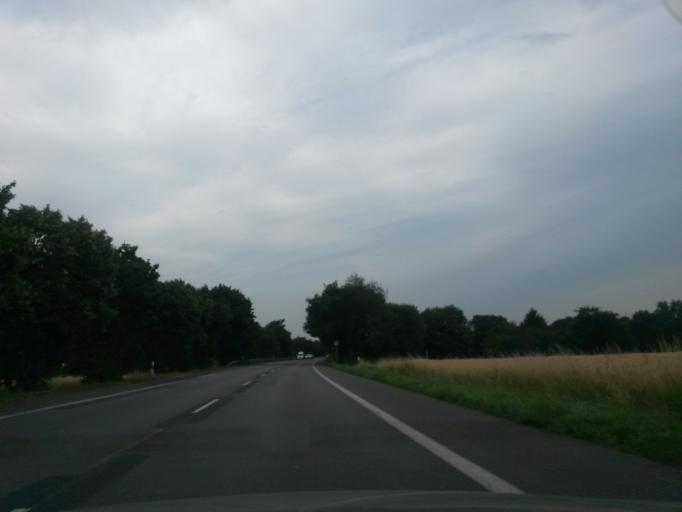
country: DE
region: North Rhine-Westphalia
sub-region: Regierungsbezirk Dusseldorf
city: Moers
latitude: 51.4569
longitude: 6.5987
